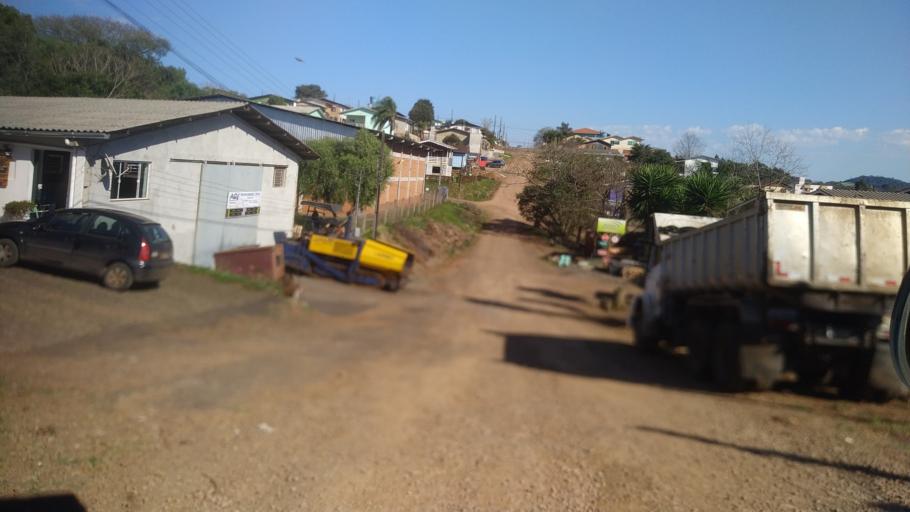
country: BR
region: Santa Catarina
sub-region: Chapeco
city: Chapeco
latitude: -27.0350
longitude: -52.6286
